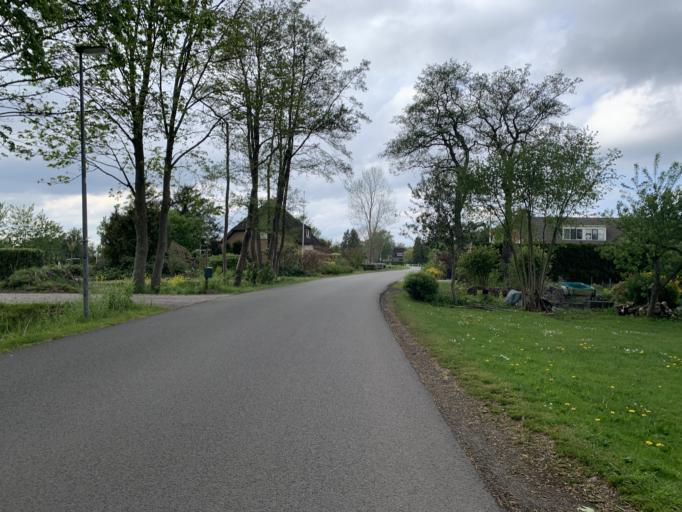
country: NL
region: Groningen
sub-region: Gemeente Haren
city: Haren
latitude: 53.2044
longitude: 6.6537
